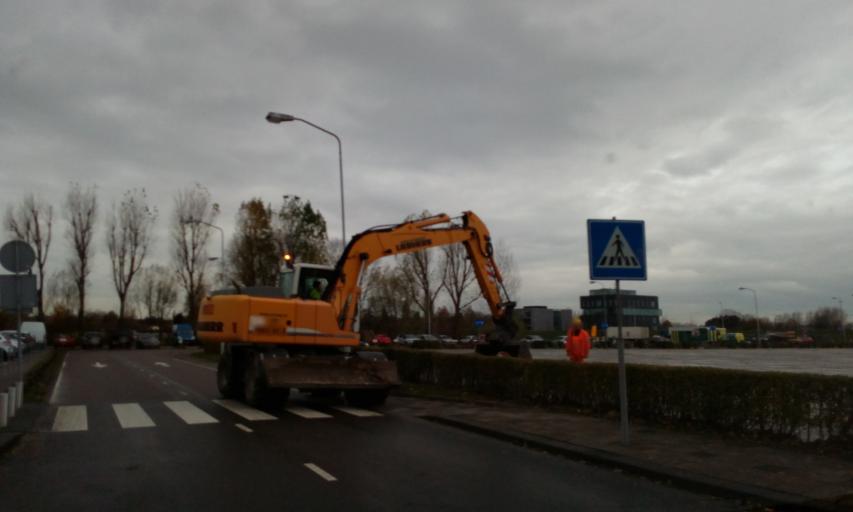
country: NL
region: South Holland
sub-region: Gemeente Rotterdam
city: Delfshaven
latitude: 51.9471
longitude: 4.4342
